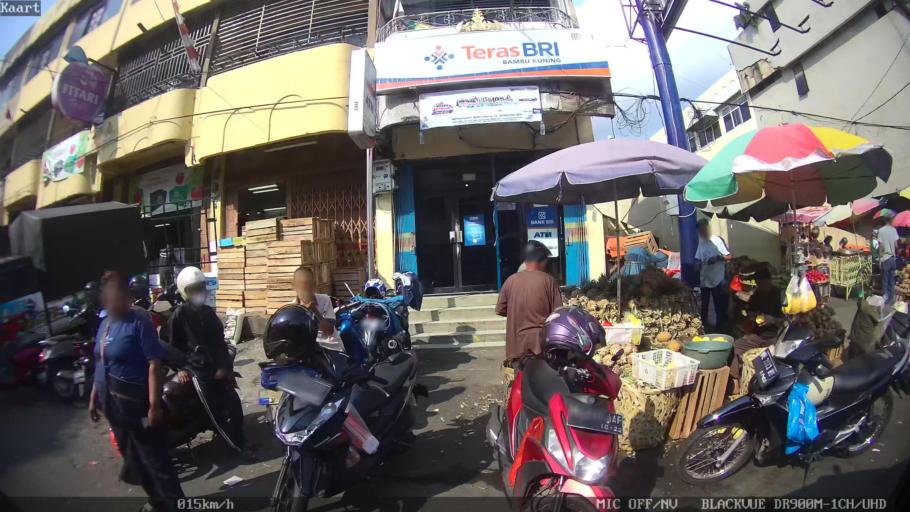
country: ID
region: Lampung
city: Bandarlampung
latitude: -5.4092
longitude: 105.2554
